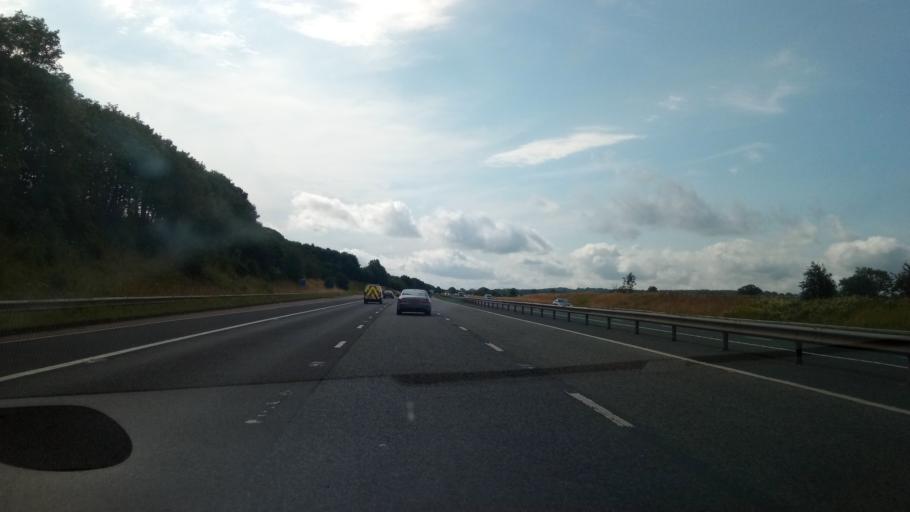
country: GB
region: England
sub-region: Cumbria
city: Penrith
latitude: 54.6343
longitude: -2.7275
